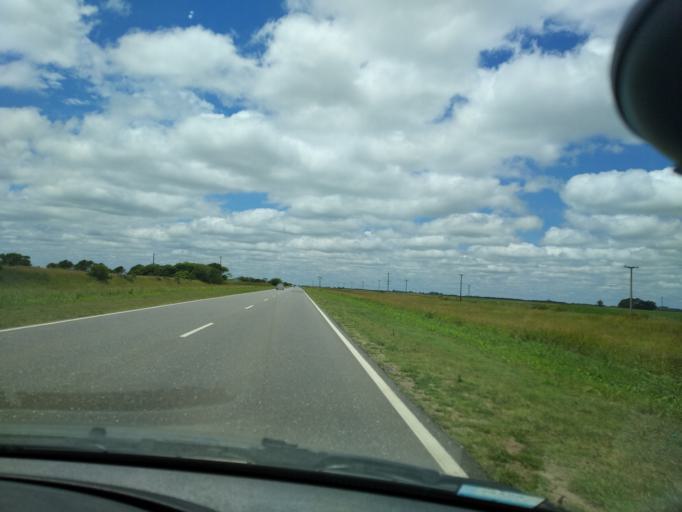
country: AR
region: Cordoba
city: Toledo
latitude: -31.6466
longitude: -64.0536
